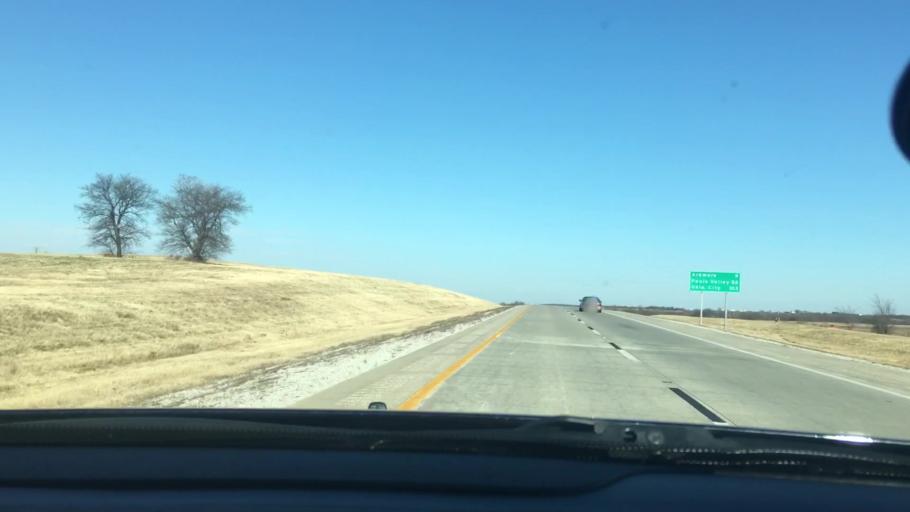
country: US
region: Oklahoma
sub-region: Carter County
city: Ardmore
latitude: 34.0836
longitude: -97.1498
